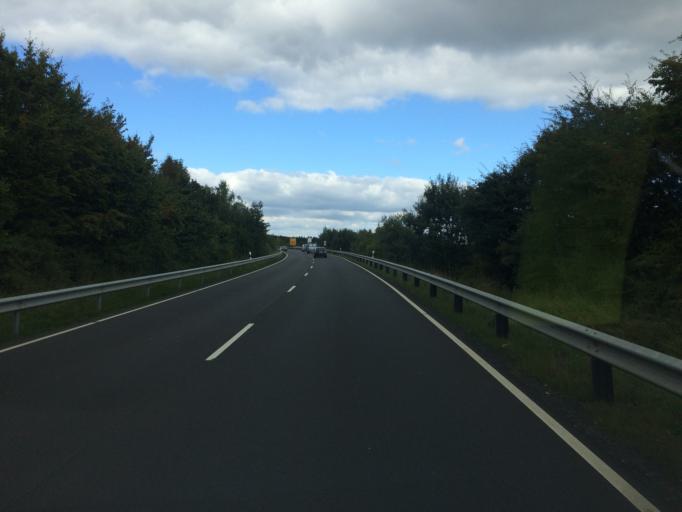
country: DE
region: Rheinland-Pfalz
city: Bretthausen
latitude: 50.6740
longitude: 8.0620
